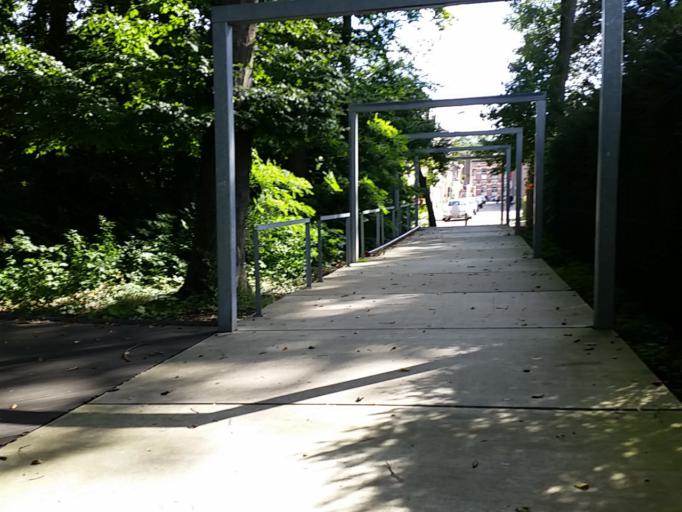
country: BE
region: Flanders
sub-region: Provincie Antwerpen
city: Schilde
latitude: 51.2406
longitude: 4.5789
